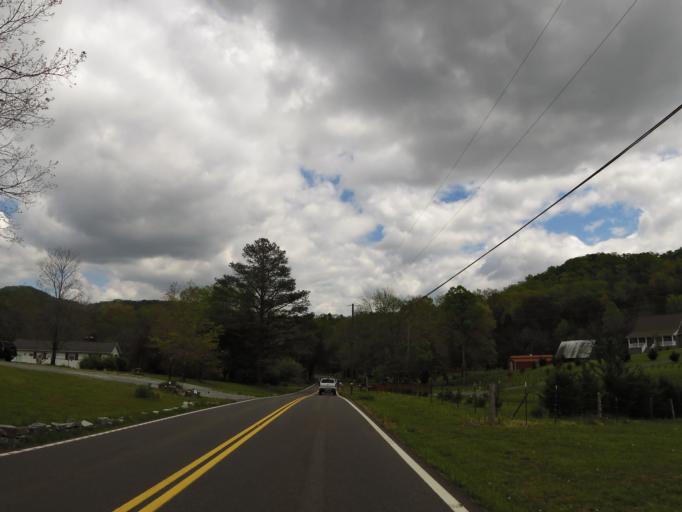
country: US
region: Tennessee
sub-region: Anderson County
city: Norris
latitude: 36.1242
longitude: -84.0005
